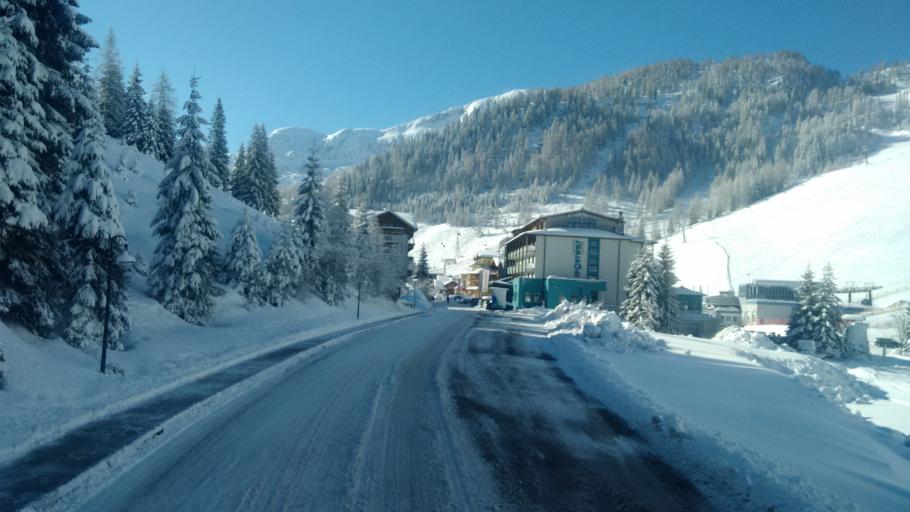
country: AT
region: Salzburg
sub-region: Politischer Bezirk Sankt Johann im Pongau
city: Untertauern
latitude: 47.2959
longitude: 13.4571
